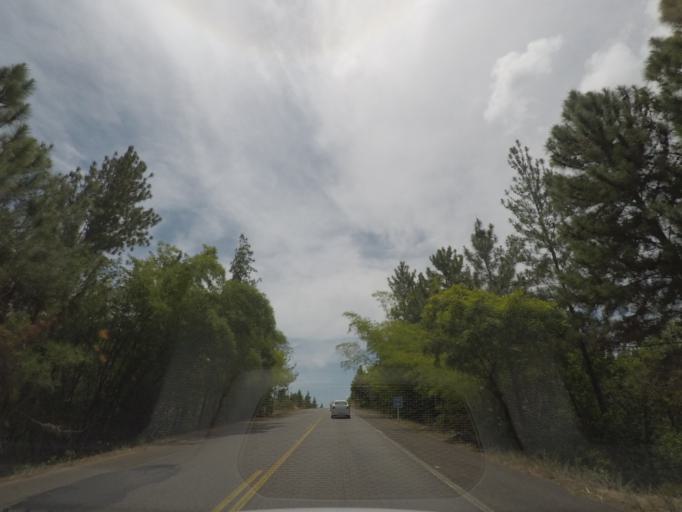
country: BR
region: Bahia
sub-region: Conde
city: Conde
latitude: -12.0000
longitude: -37.6825
